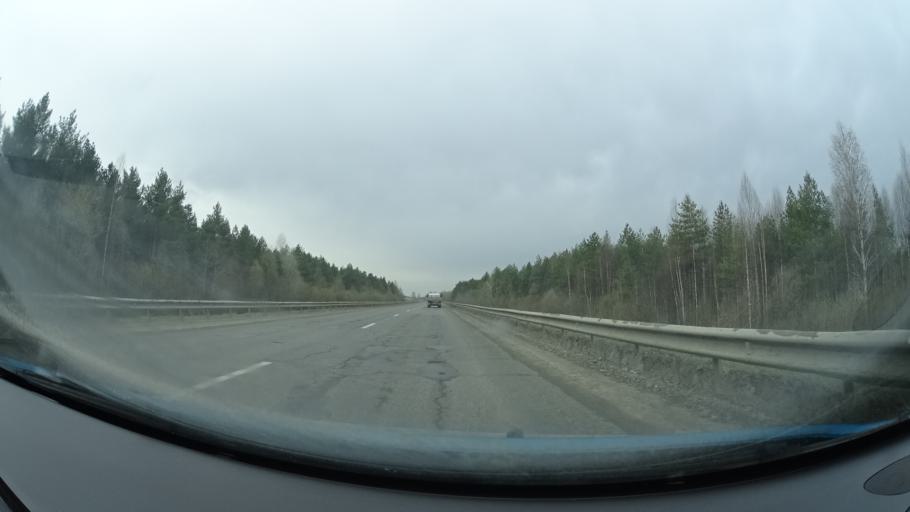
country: RU
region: Perm
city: Ust'-Kachka
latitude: 58.0828
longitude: 55.6660
